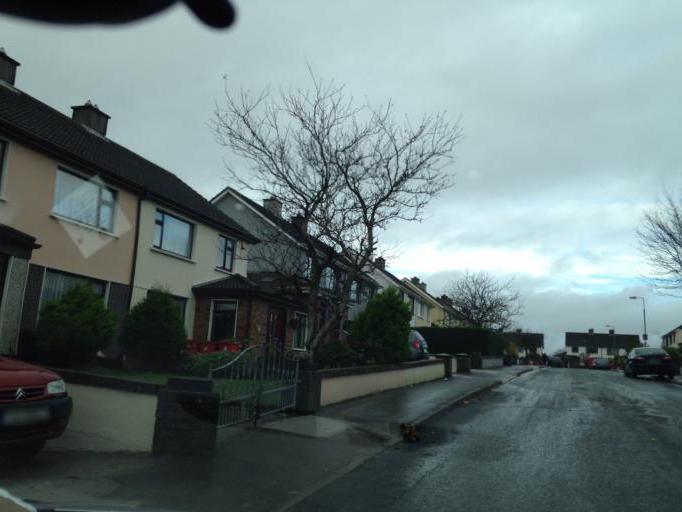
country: IE
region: Connaught
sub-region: County Galway
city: Gaillimh
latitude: 53.2729
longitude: -9.0192
